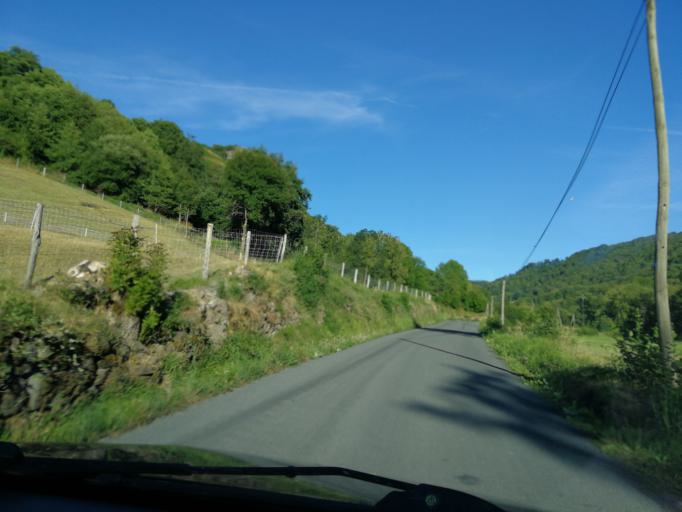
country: FR
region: Auvergne
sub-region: Departement du Cantal
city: Saint-Cernin
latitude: 45.1031
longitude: 2.5299
